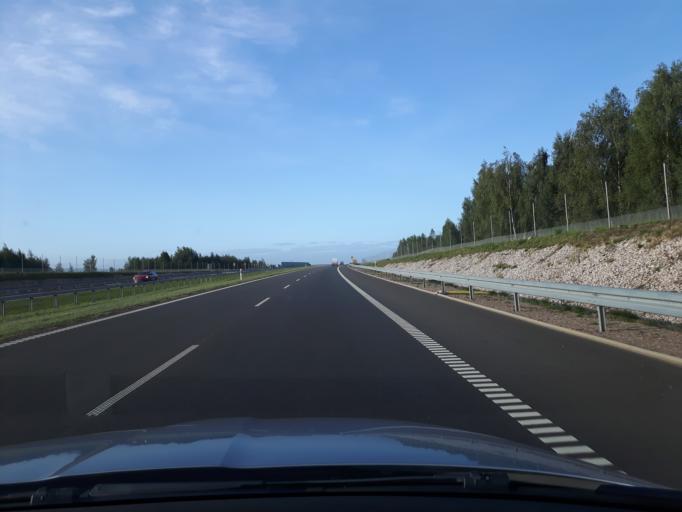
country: PL
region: Masovian Voivodeship
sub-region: Powiat radomski
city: Jedlinsk
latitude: 51.4774
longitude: 21.0597
